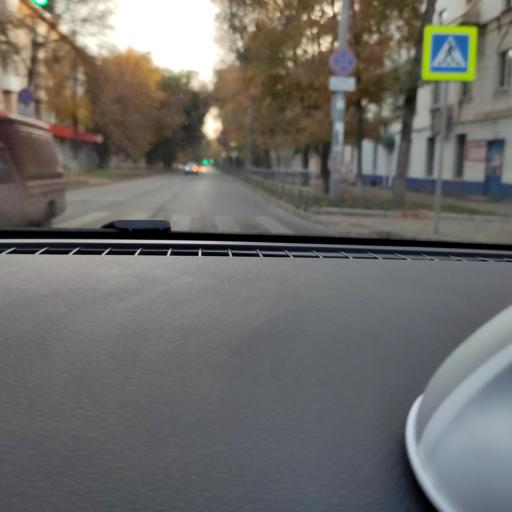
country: RU
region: Samara
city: Samara
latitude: 53.2134
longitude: 50.2402
